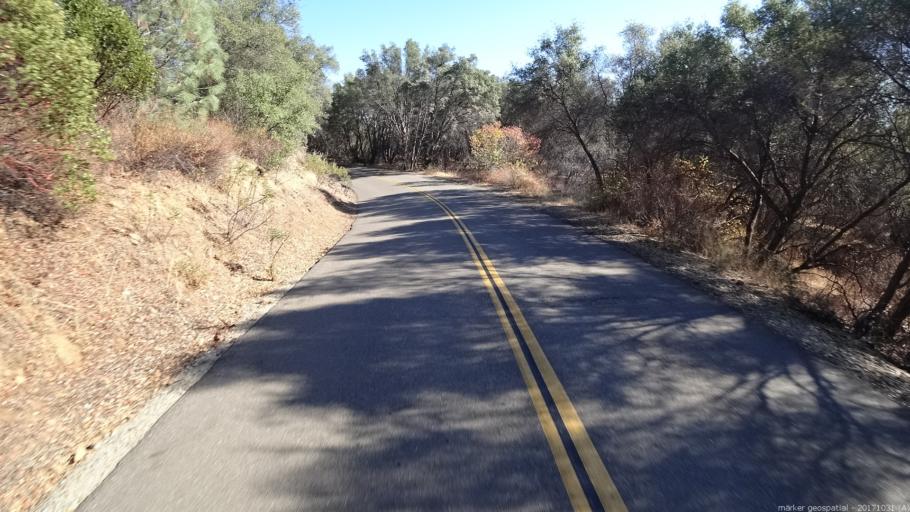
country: US
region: California
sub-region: Shasta County
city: Shingletown
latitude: 40.4416
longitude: -121.9909
